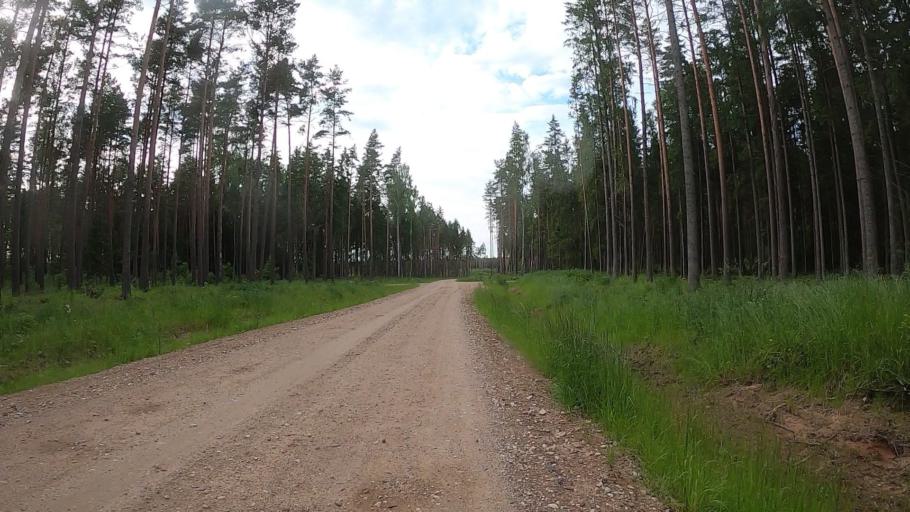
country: LV
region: Olaine
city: Olaine
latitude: 56.7655
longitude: 23.9033
